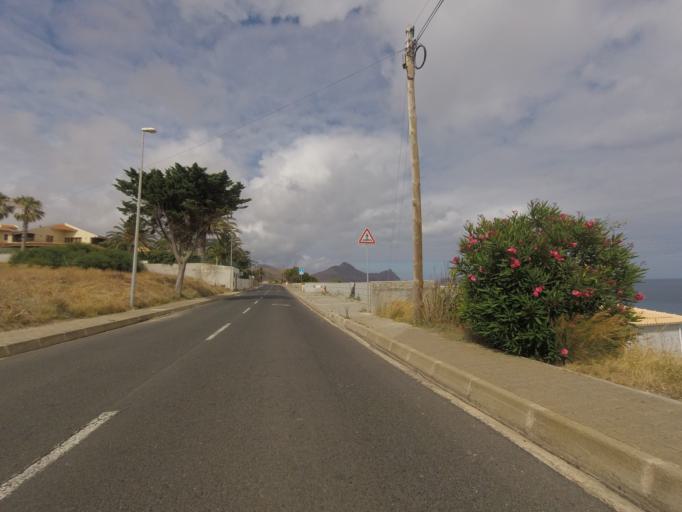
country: PT
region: Madeira
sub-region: Porto Santo
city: Vila de Porto Santo
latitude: 33.0542
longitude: -16.3440
